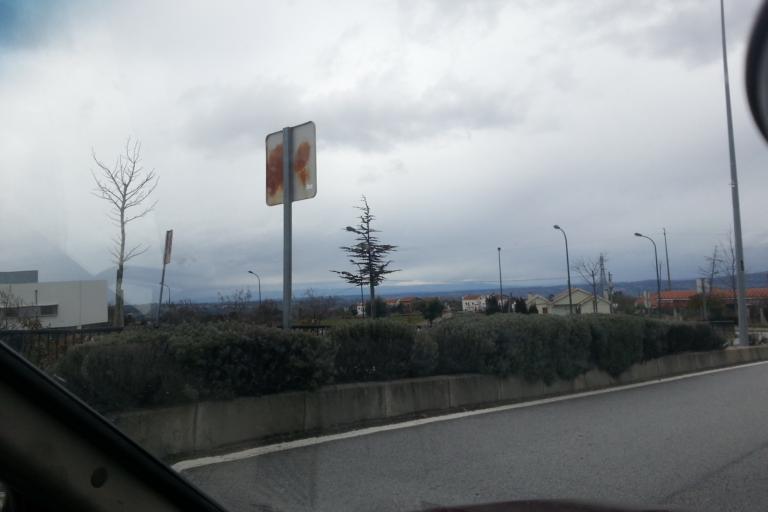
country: PT
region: Guarda
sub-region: Manteigas
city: Manteigas
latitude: 40.4941
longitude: -7.6010
